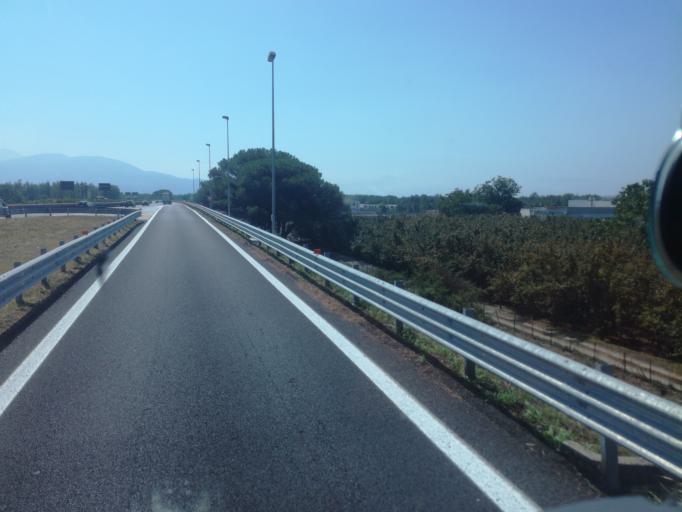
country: IT
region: Campania
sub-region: Provincia di Napoli
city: Saviano
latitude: 40.9262
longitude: 14.5002
